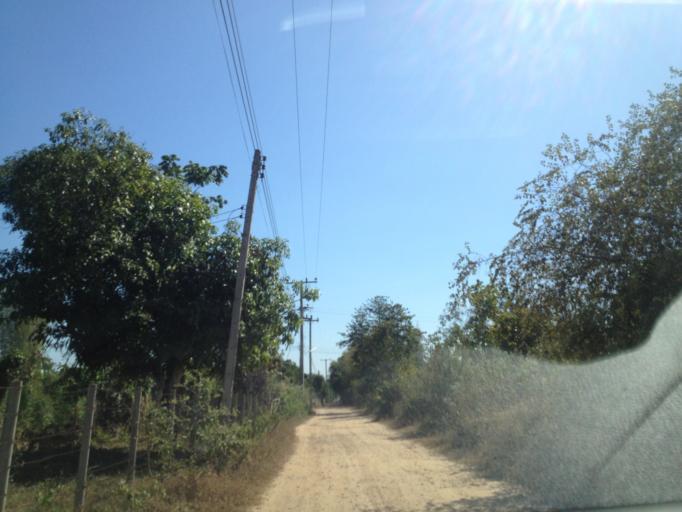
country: TH
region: Chiang Mai
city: San Pa Tong
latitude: 18.6682
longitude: 98.8724
